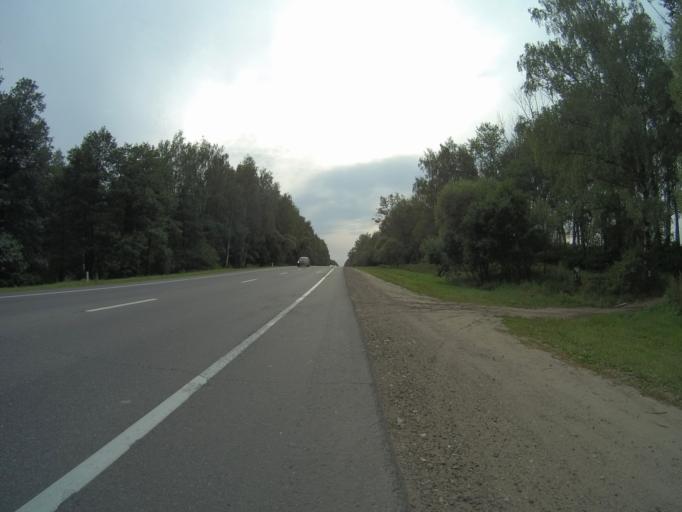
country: RU
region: Vladimir
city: Orgtrud
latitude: 56.2098
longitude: 40.6447
